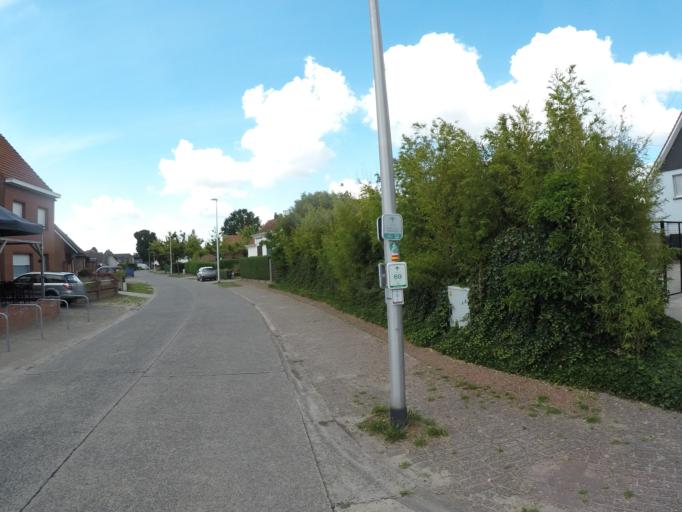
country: BE
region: Flanders
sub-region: Provincie Antwerpen
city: Vosselaar
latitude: 51.3060
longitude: 4.8792
